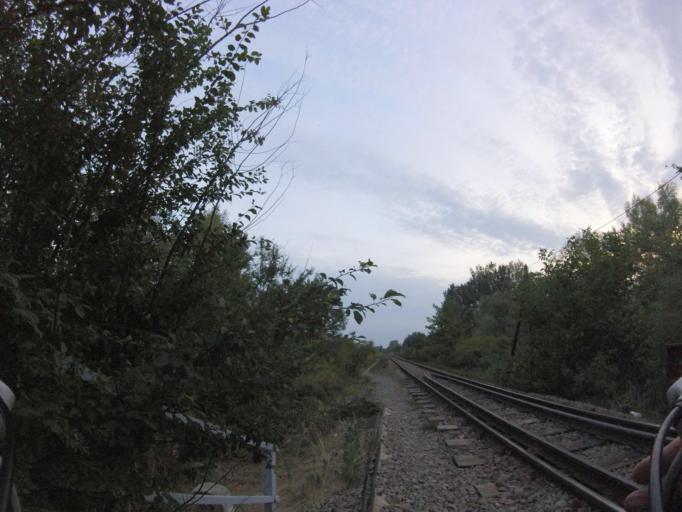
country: HU
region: Szabolcs-Szatmar-Bereg
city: Tunyogmatolcs
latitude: 47.9705
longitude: 22.4731
